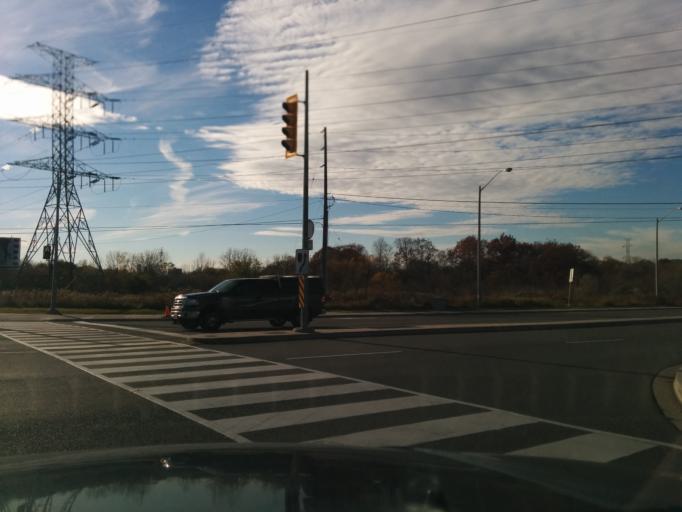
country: CA
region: Ontario
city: Etobicoke
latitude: 43.6126
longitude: -79.5626
